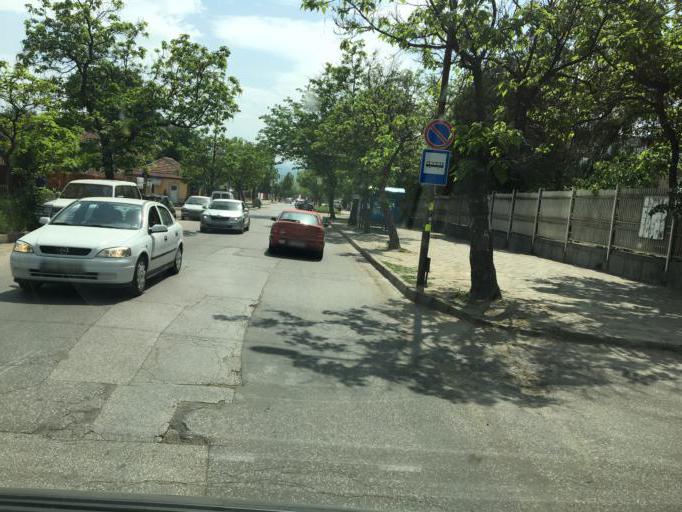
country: BG
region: Blagoevgrad
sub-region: Obshtina Blagoevgrad
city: Blagoevgrad
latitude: 42.0101
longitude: 23.0879
